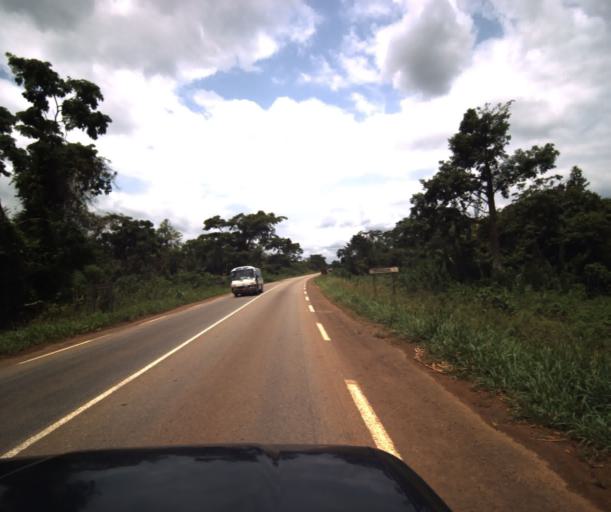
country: CM
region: Centre
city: Eseka
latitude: 3.8537
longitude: 10.9414
